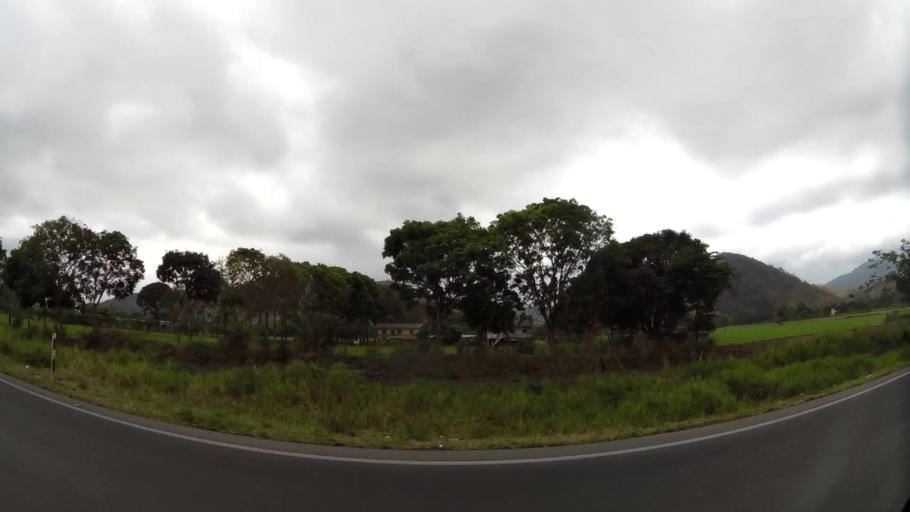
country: EC
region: Guayas
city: Coronel Marcelino Mariduena
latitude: -2.3864
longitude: -79.6309
